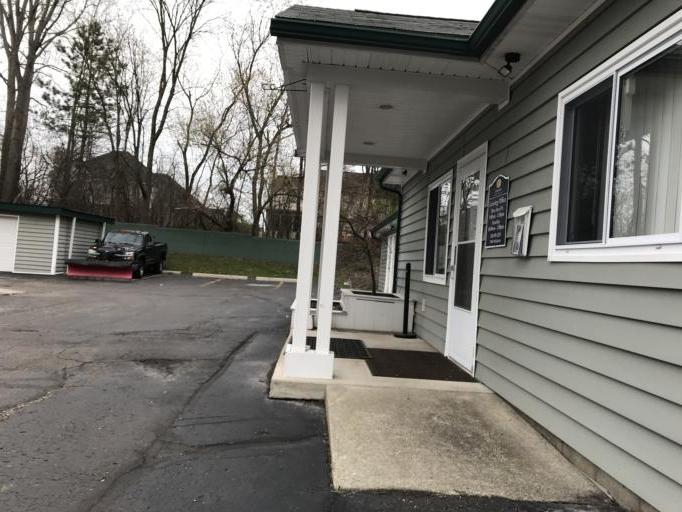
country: US
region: Michigan
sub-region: Oakland County
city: Farmington
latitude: 42.4678
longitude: -83.3350
